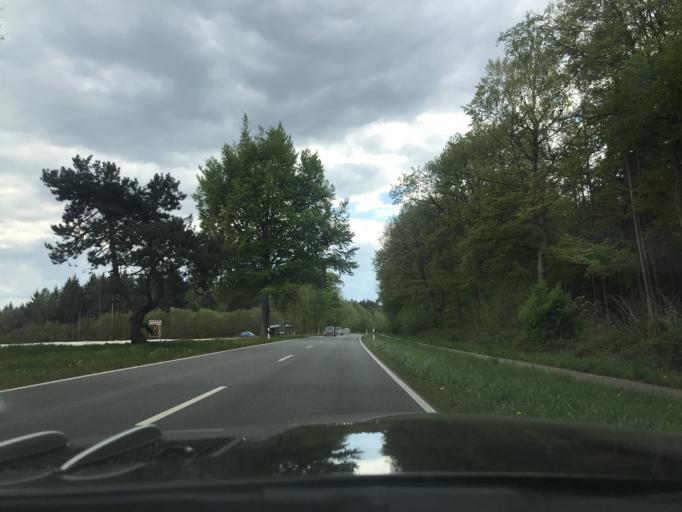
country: DE
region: Schleswig-Holstein
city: Gross Gronau
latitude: 53.7849
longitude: 10.7549
